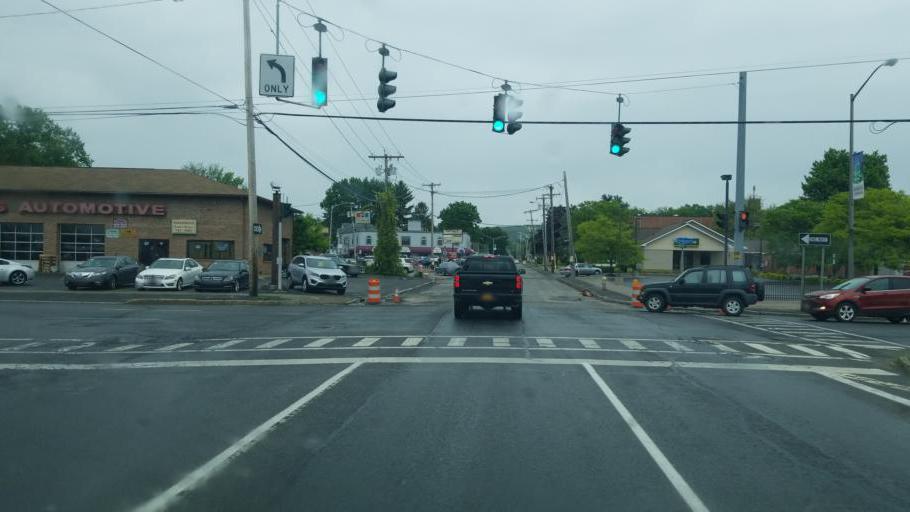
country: US
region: New York
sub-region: Oneida County
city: Utica
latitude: 43.1163
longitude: -75.2108
